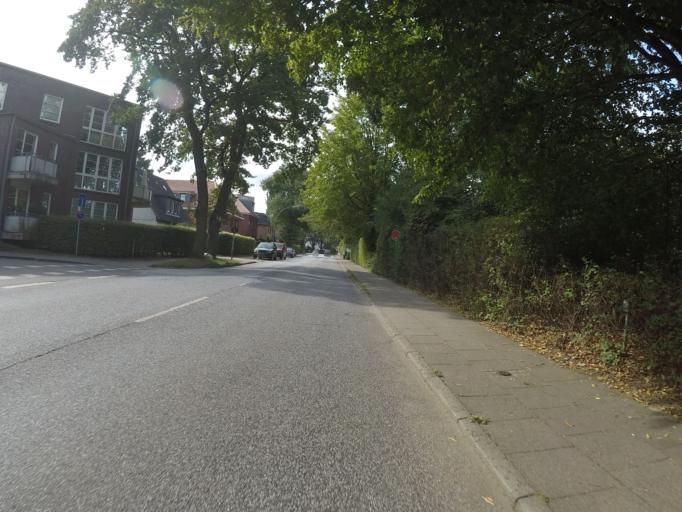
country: DE
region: Schleswig-Holstein
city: Bonningstedt
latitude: 53.6334
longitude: 9.9406
